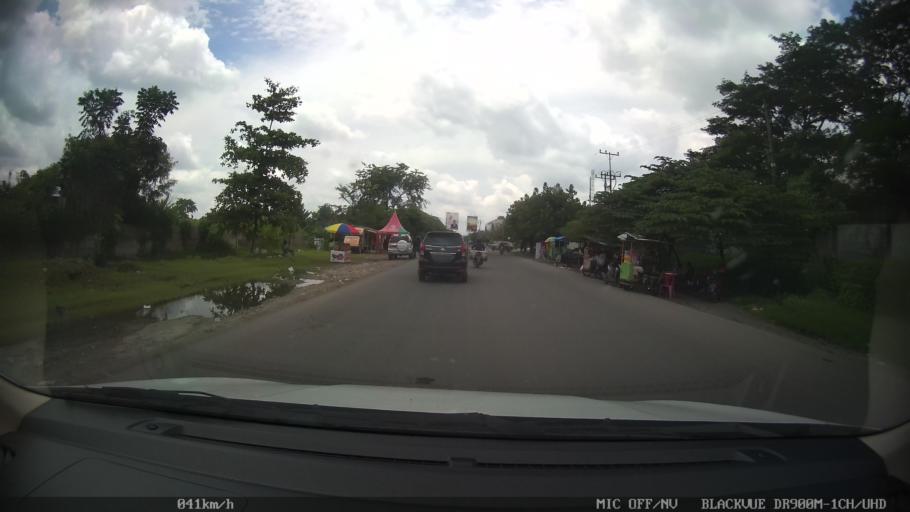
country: ID
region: North Sumatra
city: Medan
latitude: 3.6301
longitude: 98.7079
